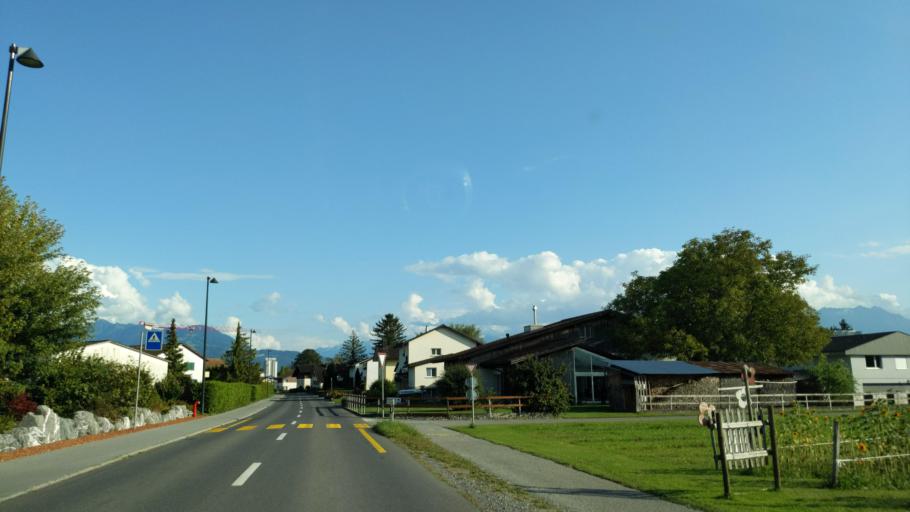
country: CH
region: Saint Gallen
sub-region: Wahlkreis Rheintal
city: Oberriet
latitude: 47.3279
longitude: 9.5636
